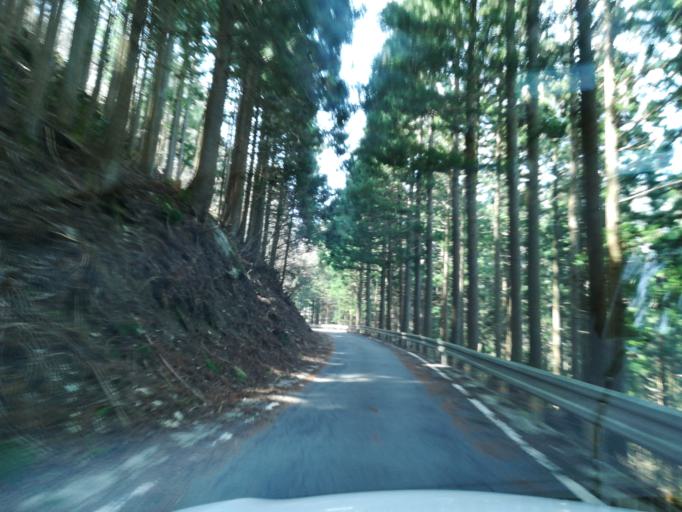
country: JP
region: Tokushima
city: Wakimachi
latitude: 33.8886
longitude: 134.0597
